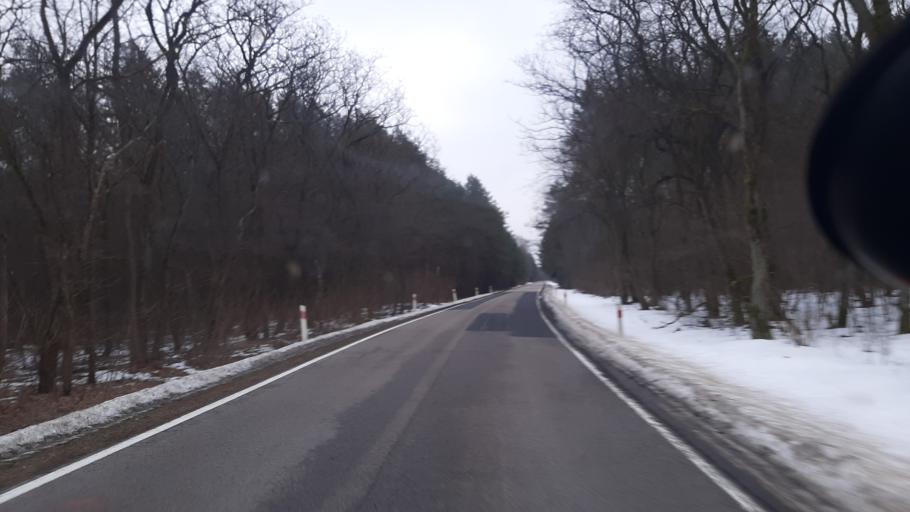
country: PL
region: Lublin Voivodeship
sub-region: Powiat wlodawski
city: Wlodawa
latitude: 51.4903
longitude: 23.6084
